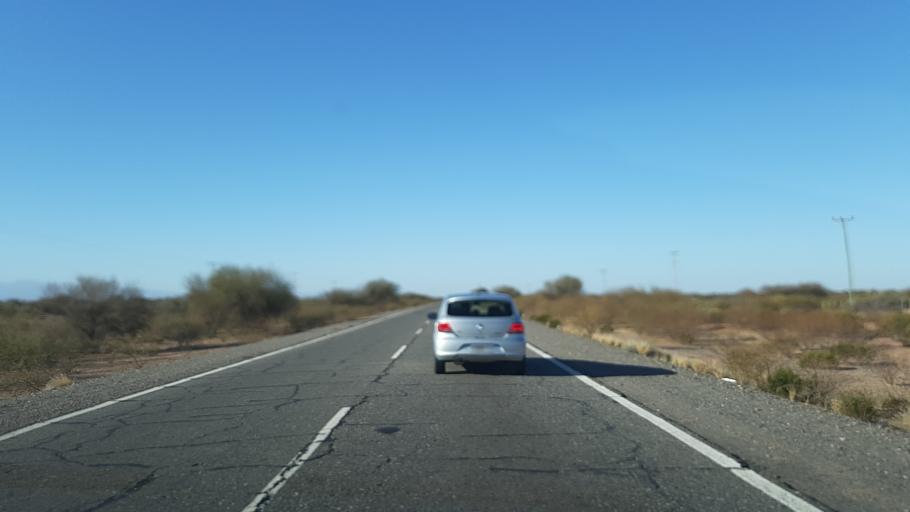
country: AR
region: San Juan
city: Caucete
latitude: -31.6082
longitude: -67.7170
